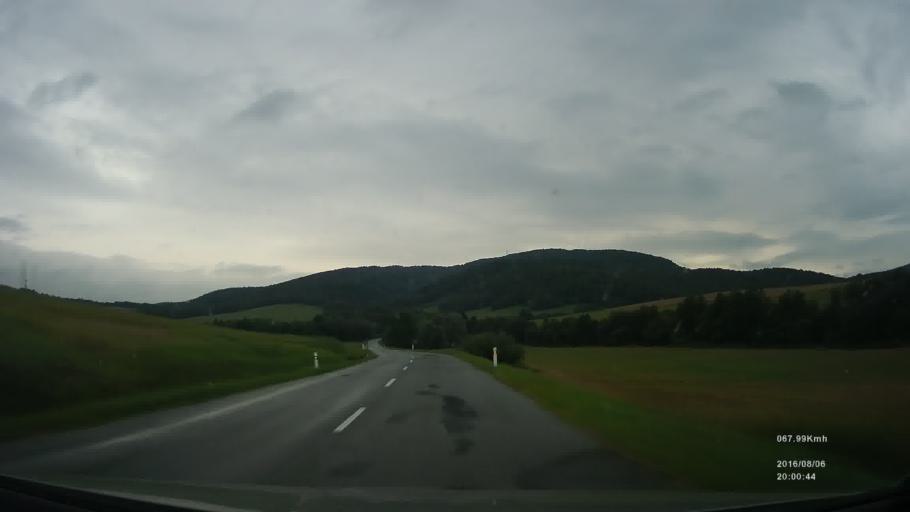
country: SK
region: Presovsky
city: Svidnik
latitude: 49.2495
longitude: 21.5830
